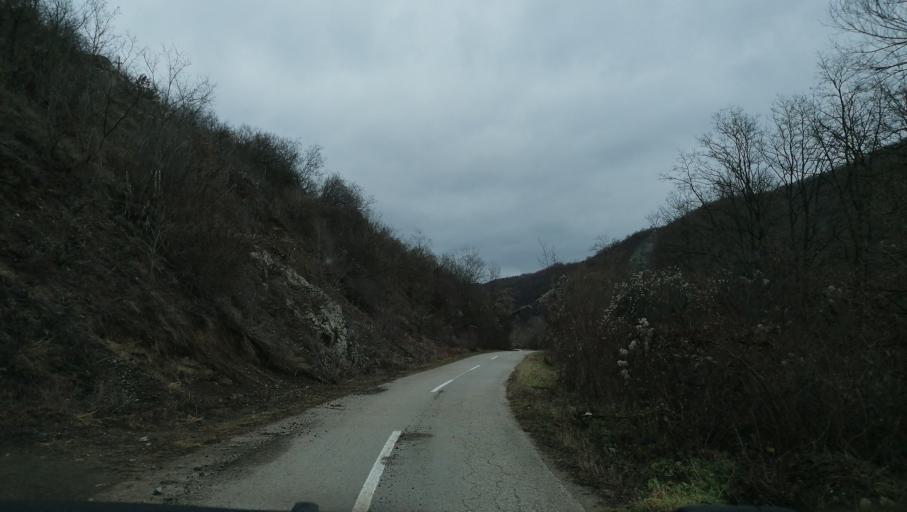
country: RS
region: Central Serbia
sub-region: Pirotski Okrug
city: Dimitrovgrad
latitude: 42.9496
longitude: 22.7699
